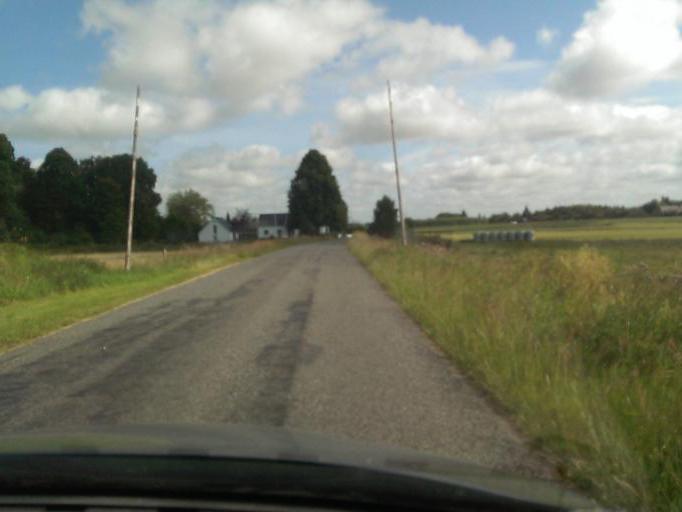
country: DK
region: North Denmark
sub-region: Alborg Kommune
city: Vestbjerg
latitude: 57.1937
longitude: 9.9272
